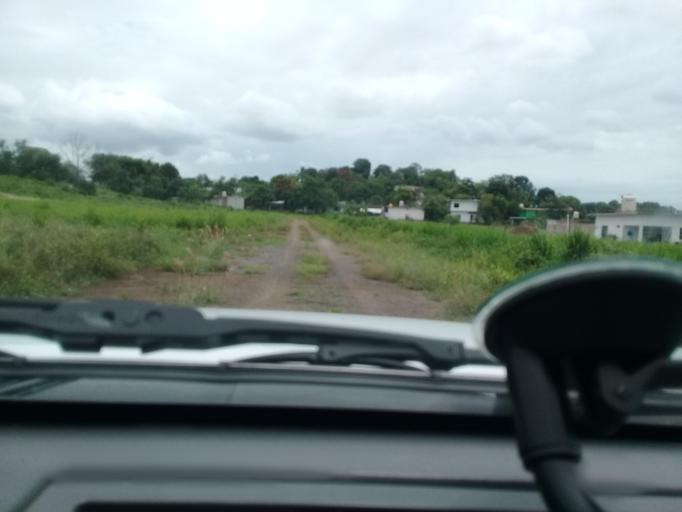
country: MX
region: Veracruz
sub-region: Paso de Ovejas
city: El Hatito
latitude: 19.2761
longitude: -96.3956
